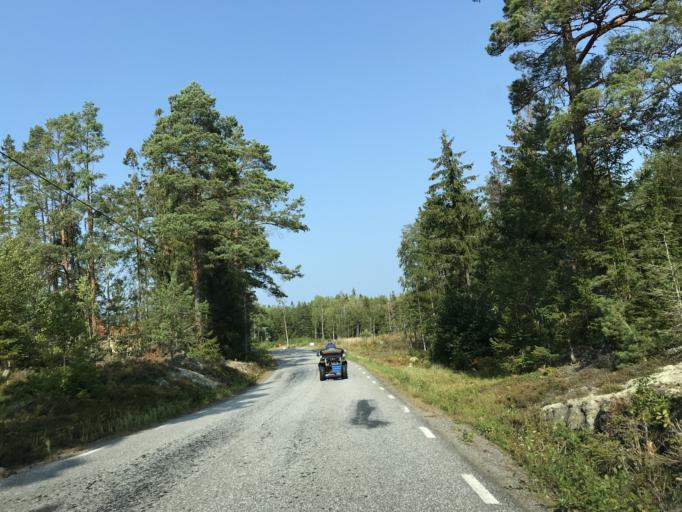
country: SE
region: Stockholm
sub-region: Norrtalje Kommun
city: Bjorko
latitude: 59.8662
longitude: 19.0472
